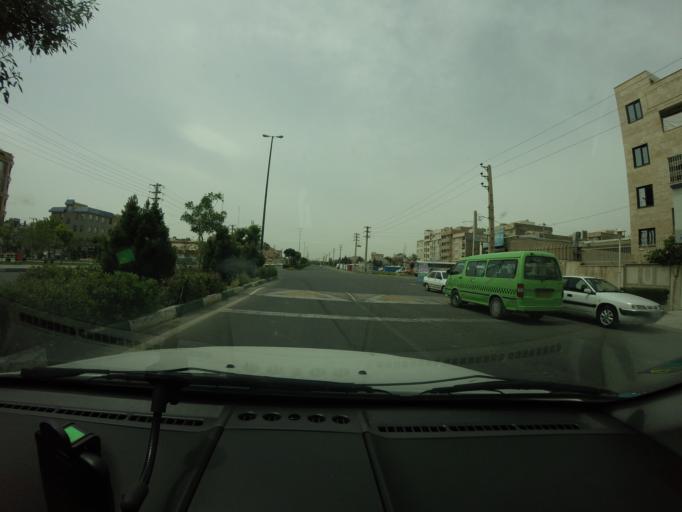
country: IR
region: Tehran
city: Eslamshahr
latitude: 35.5359
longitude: 51.2195
